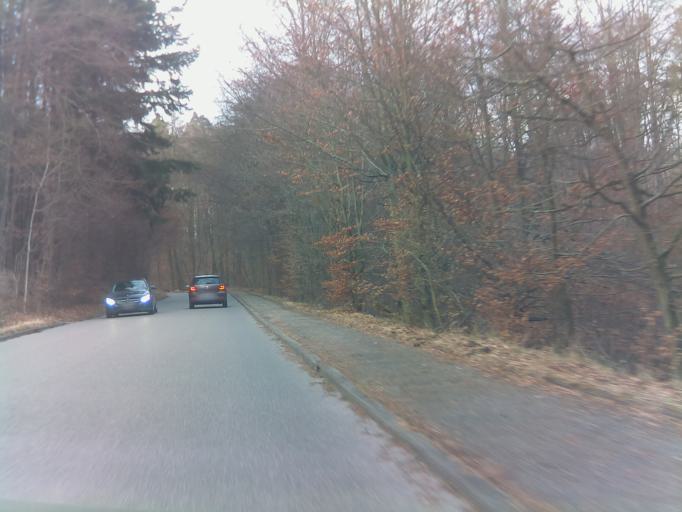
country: DE
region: Baden-Wuerttemberg
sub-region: Regierungsbezirk Stuttgart
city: Gerlingen
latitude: 48.7809
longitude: 9.0637
